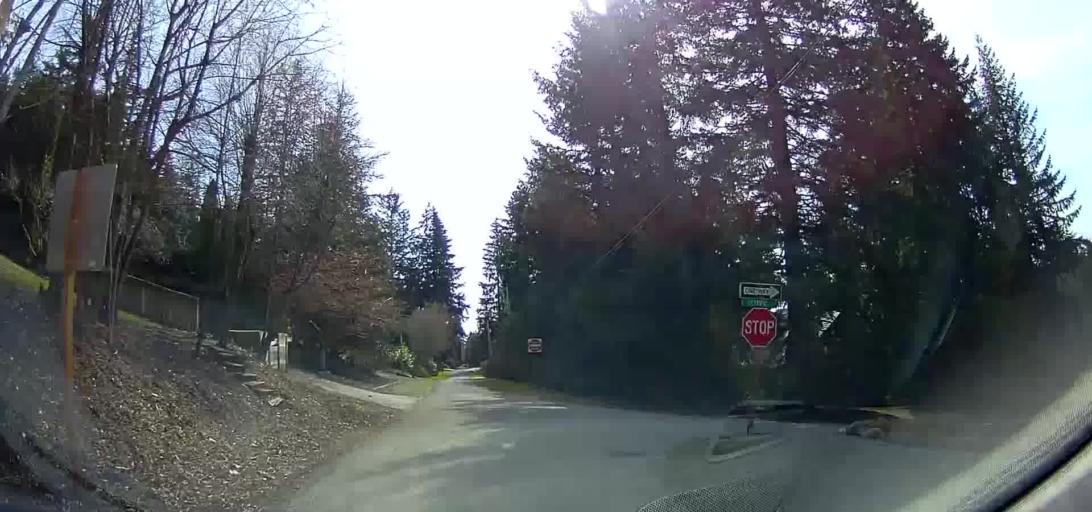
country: US
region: Washington
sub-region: Skagit County
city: Mount Vernon
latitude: 48.3971
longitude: -122.3159
